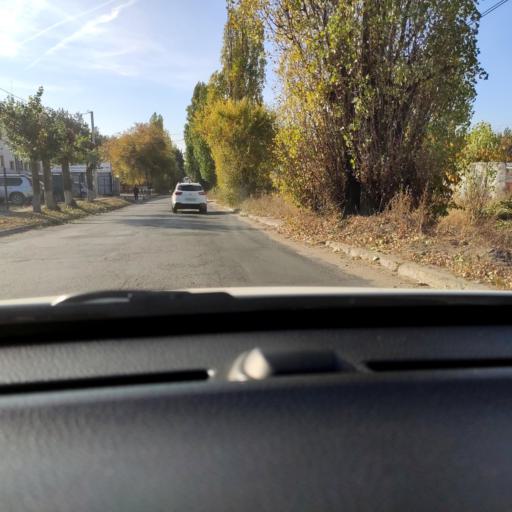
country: RU
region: Voronezj
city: Pridonskoy
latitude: 51.6461
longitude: 39.1097
